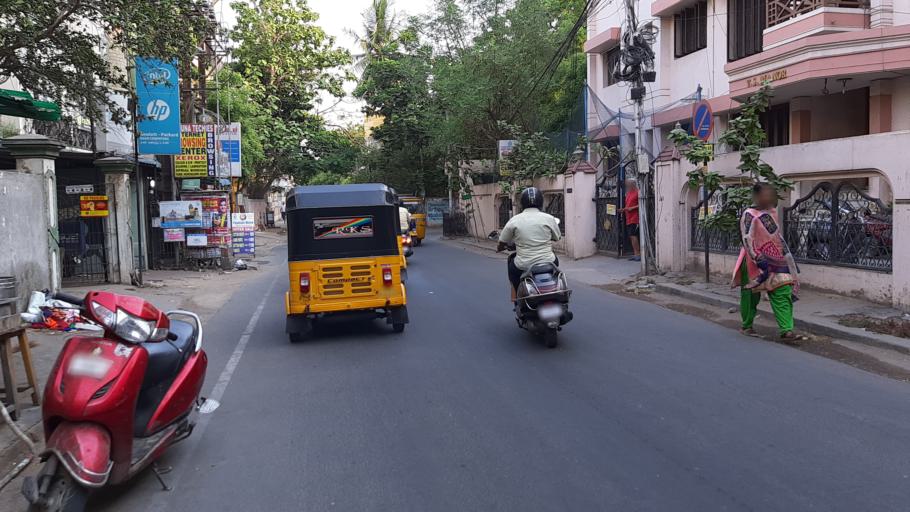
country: IN
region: Tamil Nadu
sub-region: Chennai
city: Gandhi Nagar
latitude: 13.0345
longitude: 80.2331
